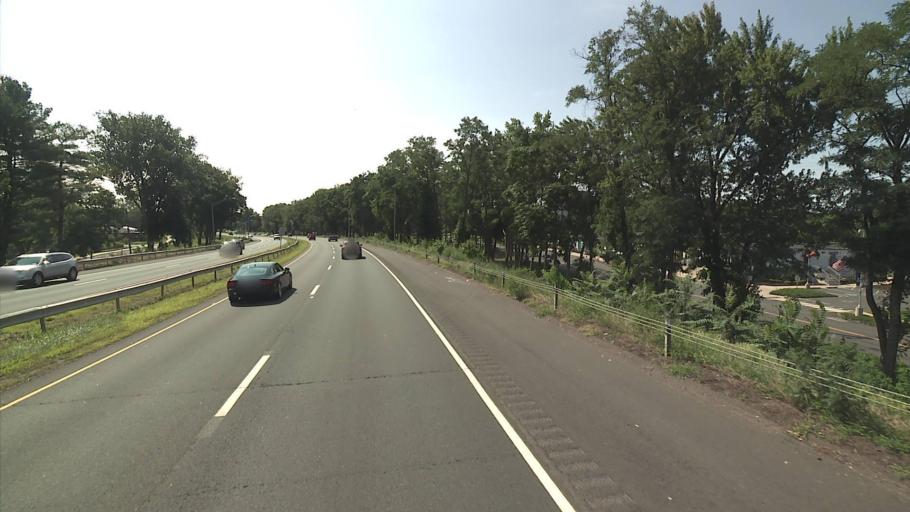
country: US
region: Connecticut
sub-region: Hartford County
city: Wethersfield
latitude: 41.7456
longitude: -72.6410
